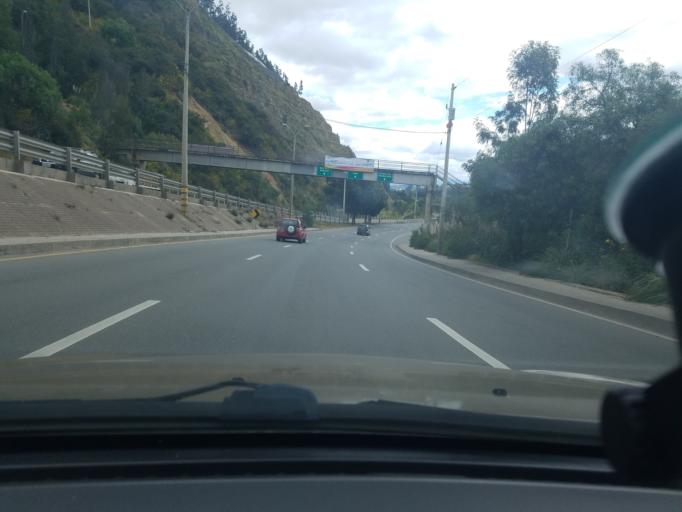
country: EC
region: Azuay
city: Llacao
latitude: -2.8625
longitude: -78.9288
